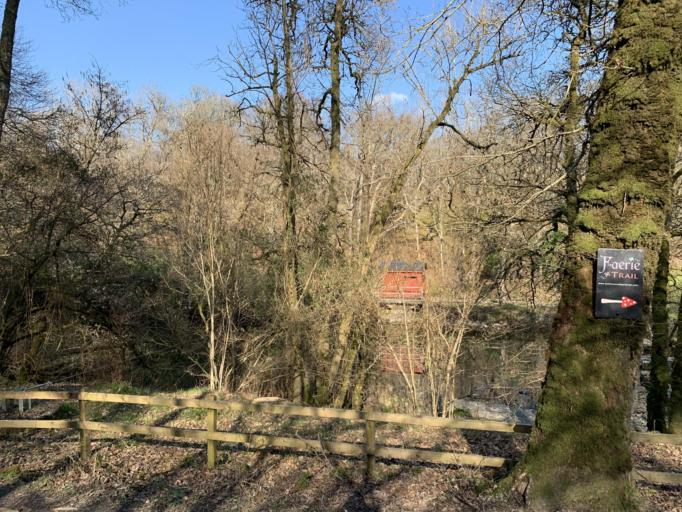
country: GB
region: Scotland
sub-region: West Dunbartonshire
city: Balloch
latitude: 56.1002
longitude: -4.6447
